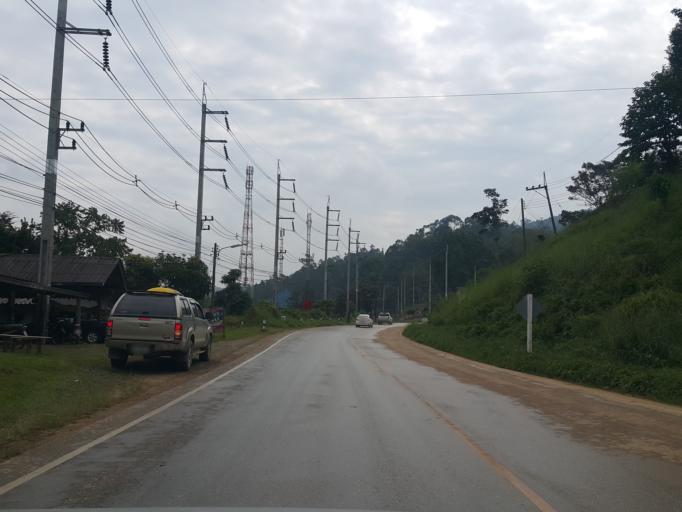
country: TH
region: Chiang Mai
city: Mae Taeng
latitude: 19.1648
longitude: 98.6906
